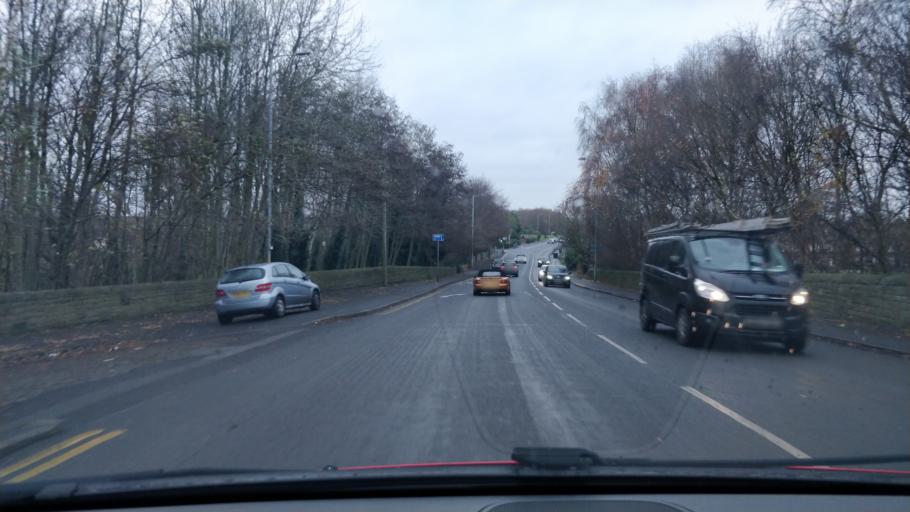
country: GB
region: England
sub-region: Sefton
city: Thornton
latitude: 53.4860
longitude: -2.9935
